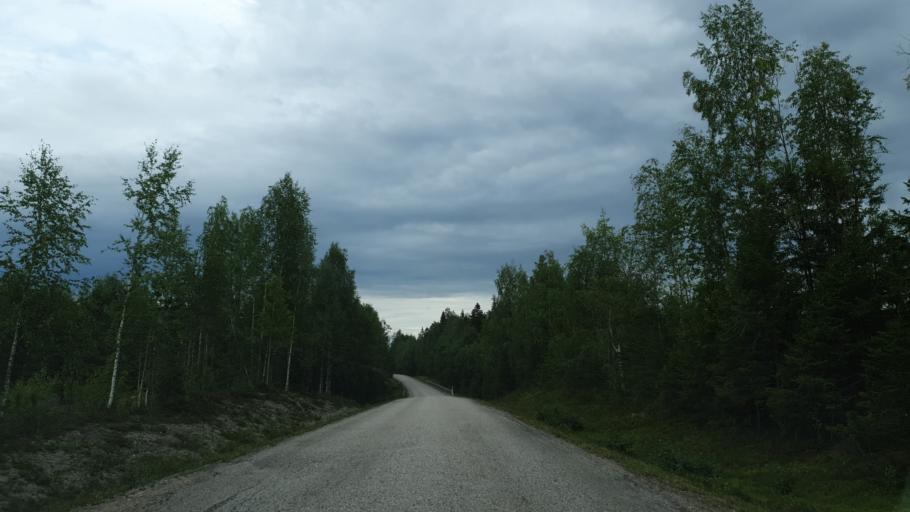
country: FI
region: Kainuu
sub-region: Kehys-Kainuu
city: Kuhmo
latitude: 64.3381
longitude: 29.3554
